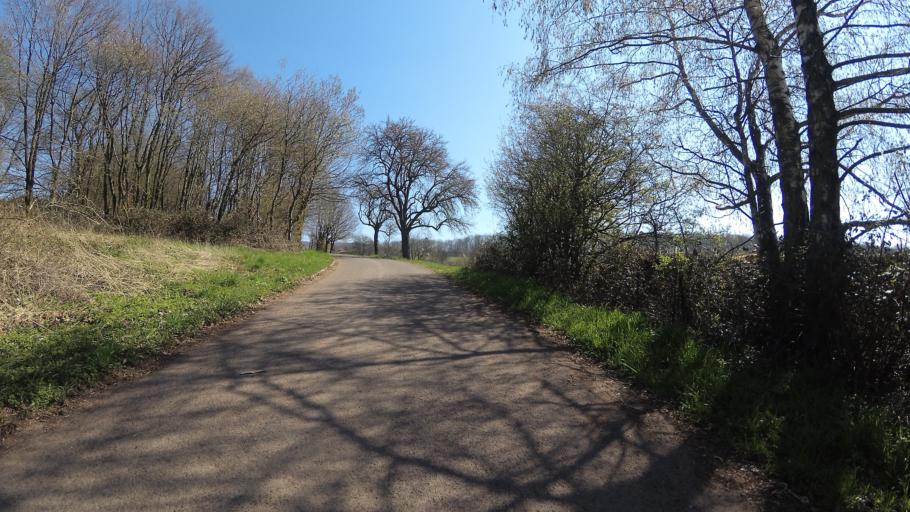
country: DE
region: Rheinland-Pfalz
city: Breitenbach
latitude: 49.4130
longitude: 7.2466
